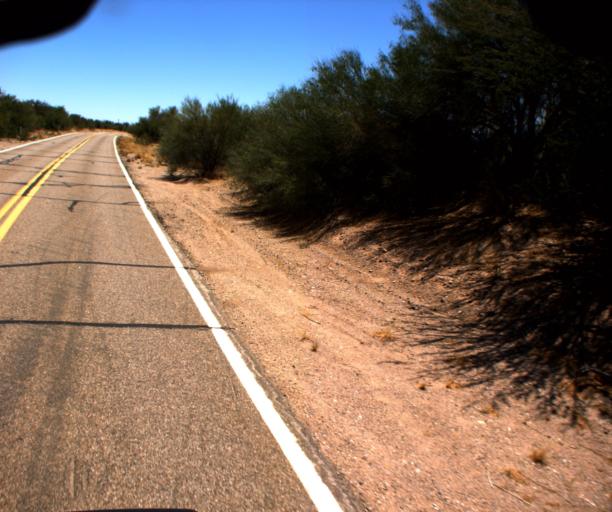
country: US
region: Arizona
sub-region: Pima County
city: Three Points
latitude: 31.8877
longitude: -111.3939
